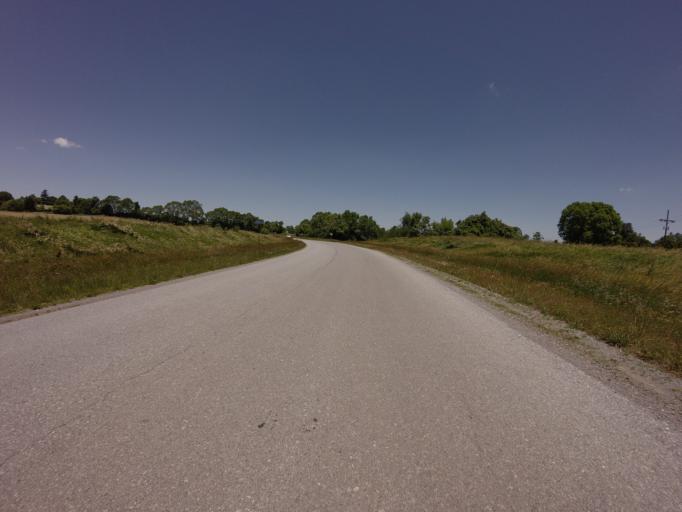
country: US
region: West Virginia
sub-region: Jefferson County
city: Bolivar
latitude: 39.3136
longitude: -77.7740
